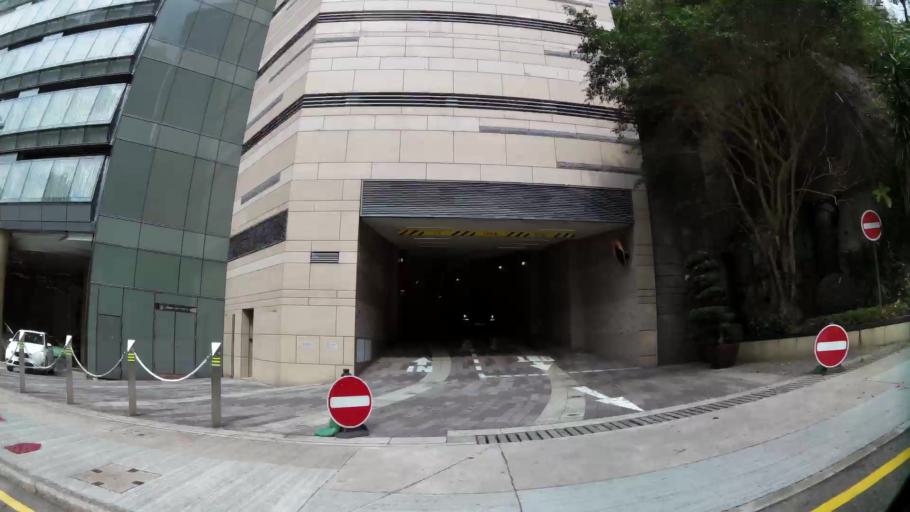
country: HK
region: Wanchai
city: Wan Chai
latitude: 22.2765
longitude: 114.1954
